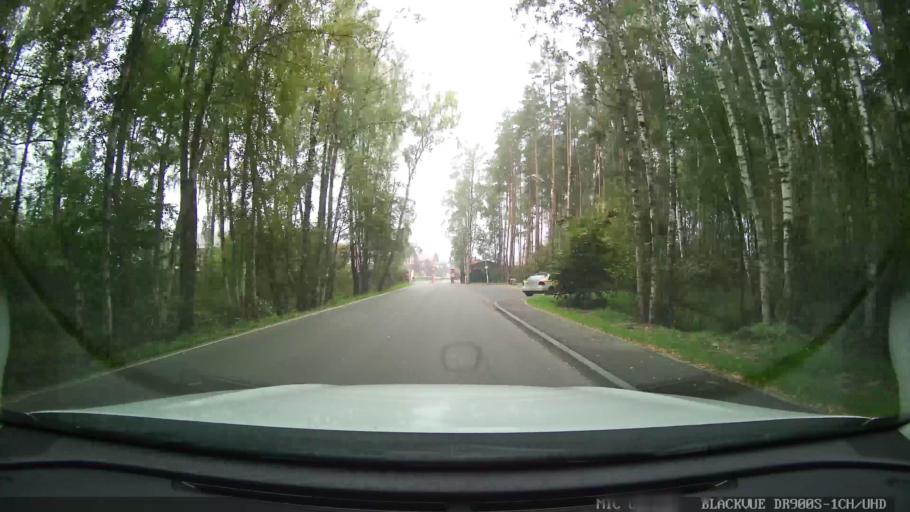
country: RU
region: Moscow
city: Novo-Peredelkino
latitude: 55.6179
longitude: 37.3269
